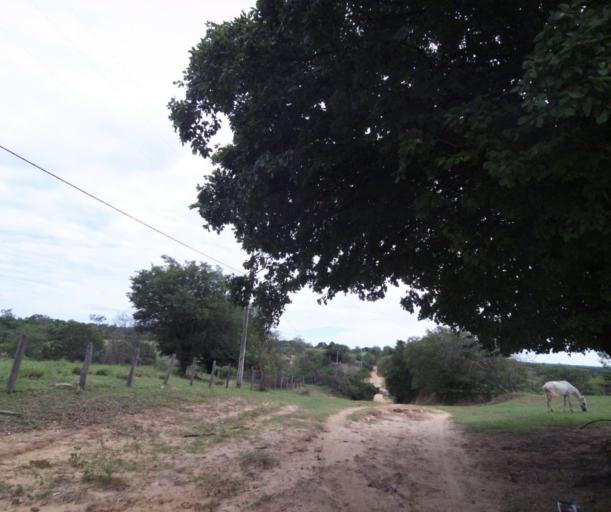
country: BR
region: Bahia
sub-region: Carinhanha
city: Carinhanha
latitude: -14.2497
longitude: -44.3502
